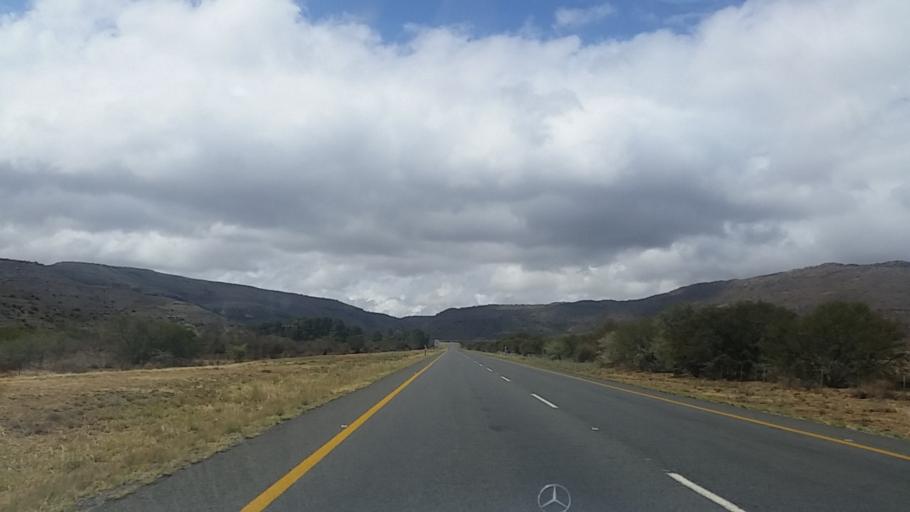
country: ZA
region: Eastern Cape
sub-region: Cacadu District Municipality
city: Graaff-Reinet
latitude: -31.9836
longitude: 24.6955
